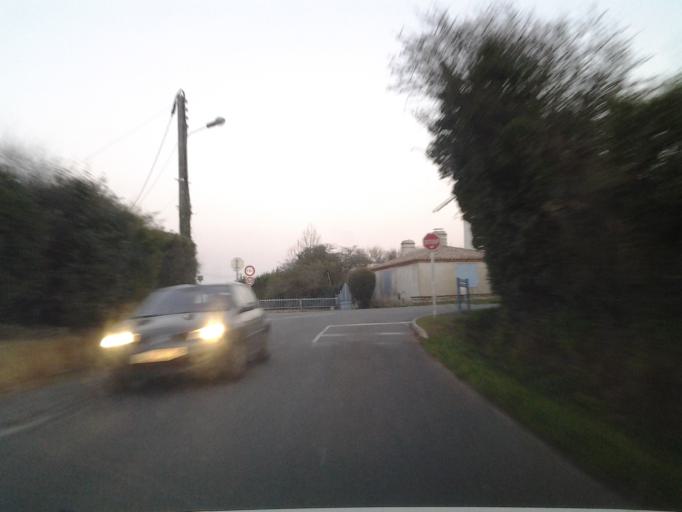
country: FR
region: Pays de la Loire
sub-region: Departement de la Vendee
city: Beauvoir-sur-Mer
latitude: 46.9084
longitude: -2.0334
